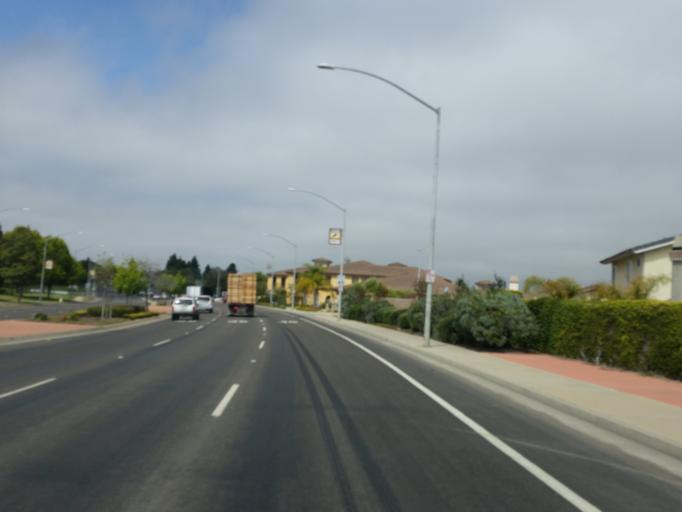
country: US
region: California
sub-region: Santa Barbara County
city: Santa Maria
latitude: 34.9234
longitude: -120.4289
